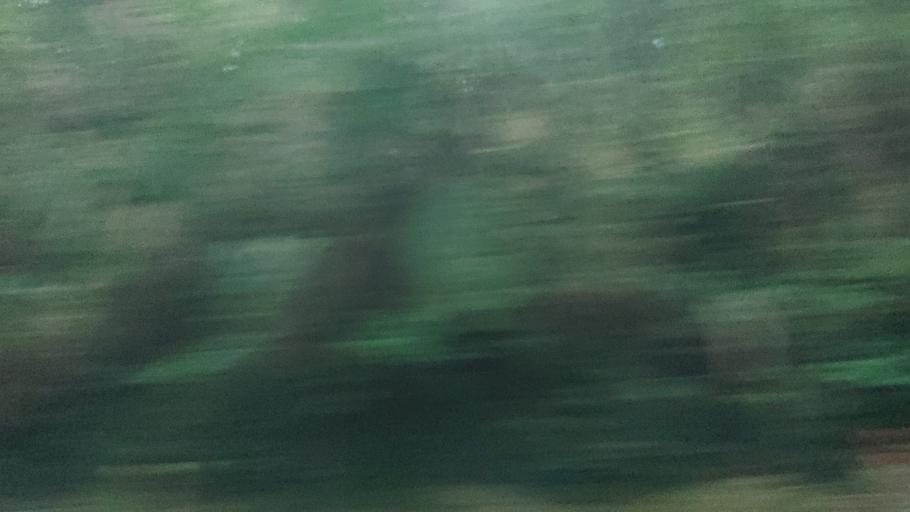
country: TW
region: Taiwan
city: Lugu
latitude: 23.5066
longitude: 120.6965
